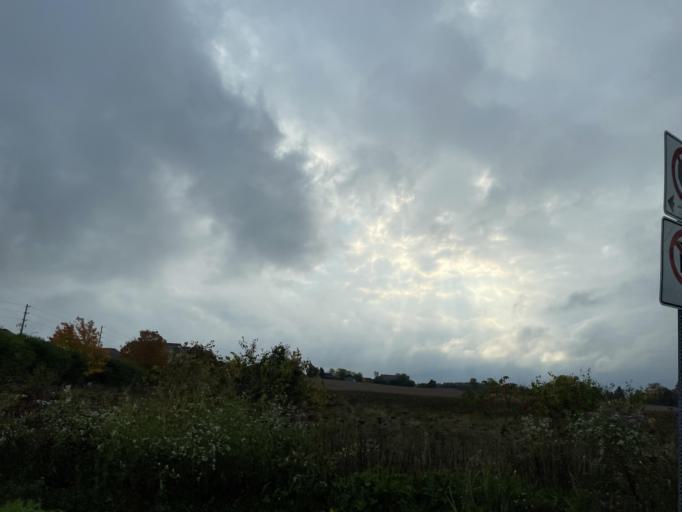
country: CA
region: Ontario
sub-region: Wellington County
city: Guelph
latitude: 43.5243
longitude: -80.1860
